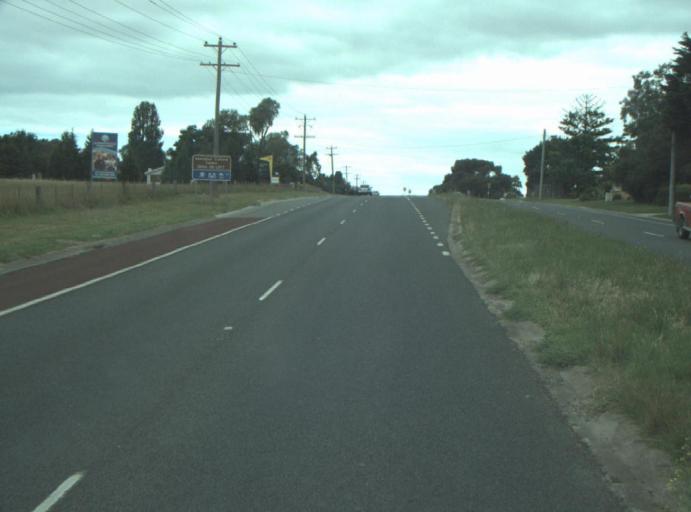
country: AU
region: Victoria
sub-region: Greater Geelong
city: Breakwater
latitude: -38.2142
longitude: 144.3389
